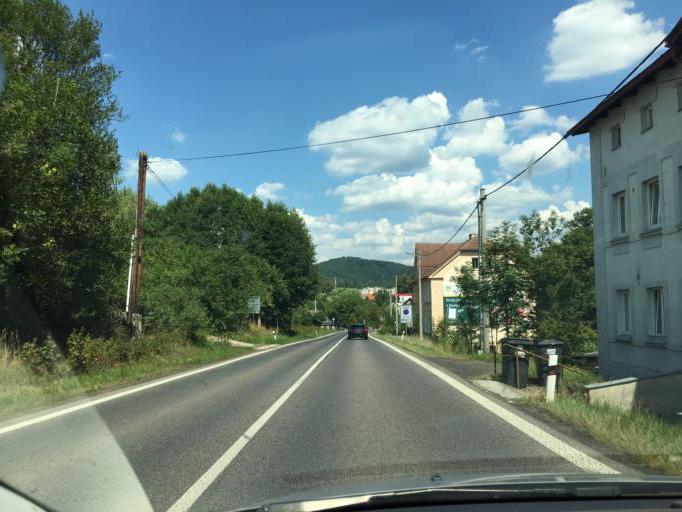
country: CZ
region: Ustecky
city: Ceska Kamenice
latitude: 50.7953
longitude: 14.4005
